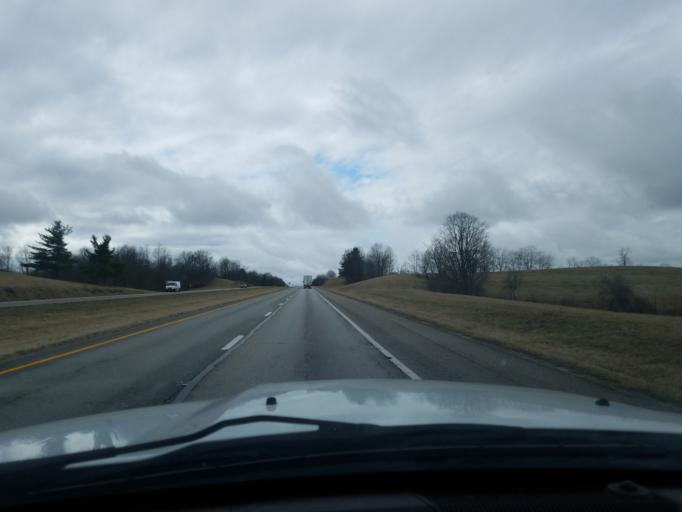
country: US
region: Kentucky
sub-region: Clark County
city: Winchester
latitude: 38.0243
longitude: -84.1238
